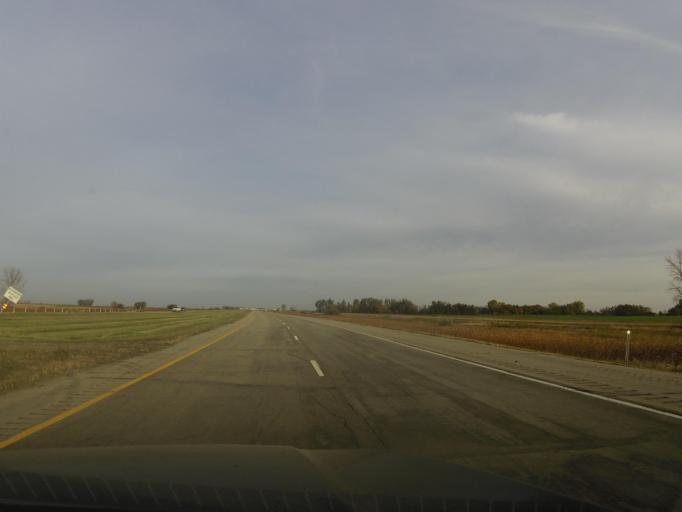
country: US
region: Minnesota
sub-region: Kittson County
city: Hallock
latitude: 48.7674
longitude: -97.2133
